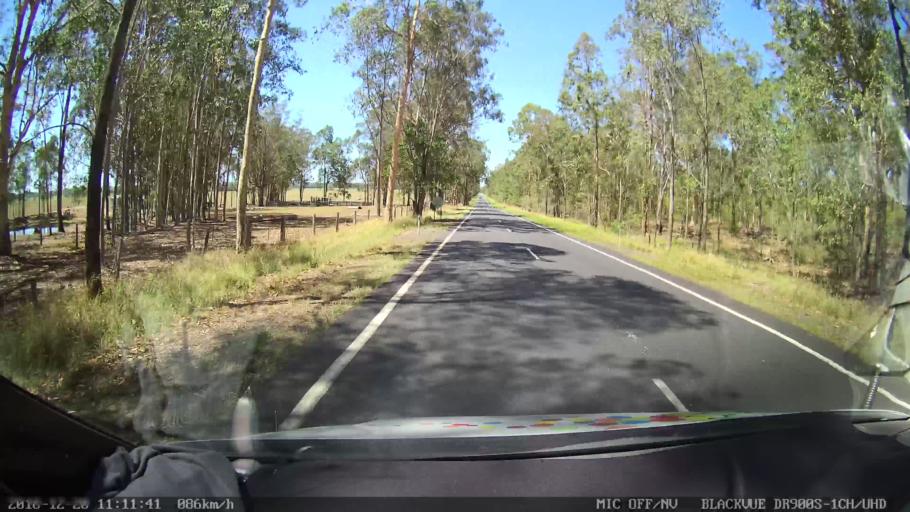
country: AU
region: New South Wales
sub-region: Richmond Valley
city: Casino
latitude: -28.9641
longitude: 153.0131
